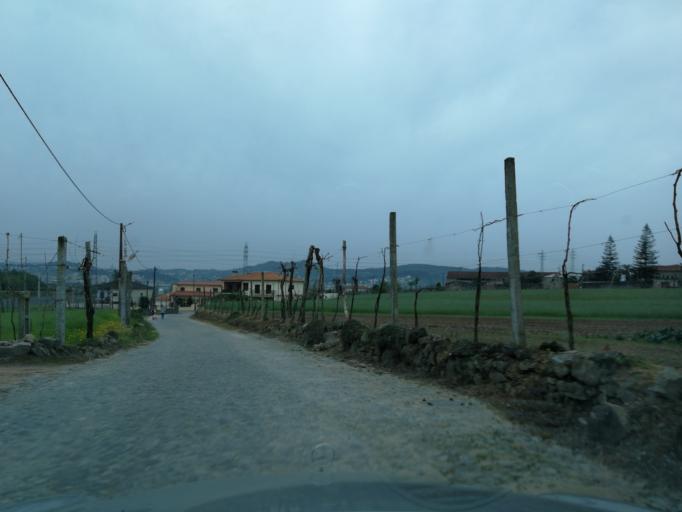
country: PT
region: Braga
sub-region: Braga
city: Braga
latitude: 41.5775
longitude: -8.4397
